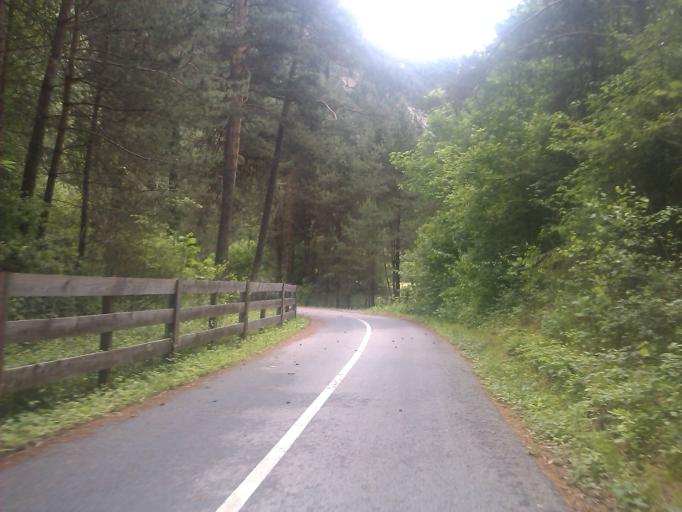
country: AT
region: Tyrol
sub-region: Politischer Bezirk Landeck
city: Fiss
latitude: 47.0358
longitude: 10.6306
